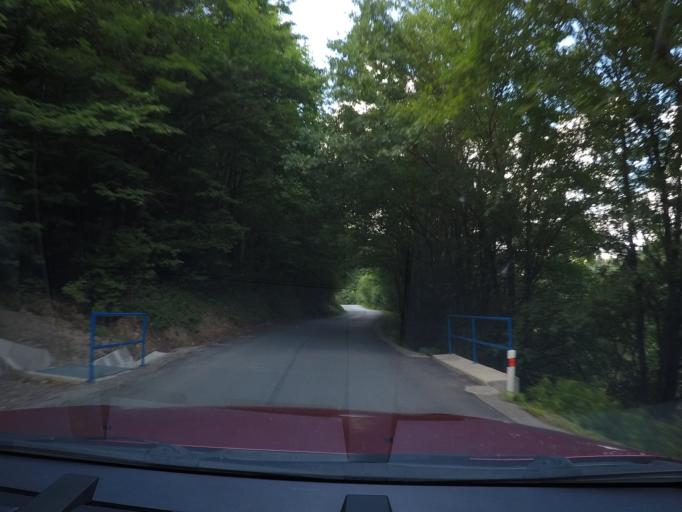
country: SK
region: Kosicky
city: Gelnica
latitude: 48.9109
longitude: 21.0872
